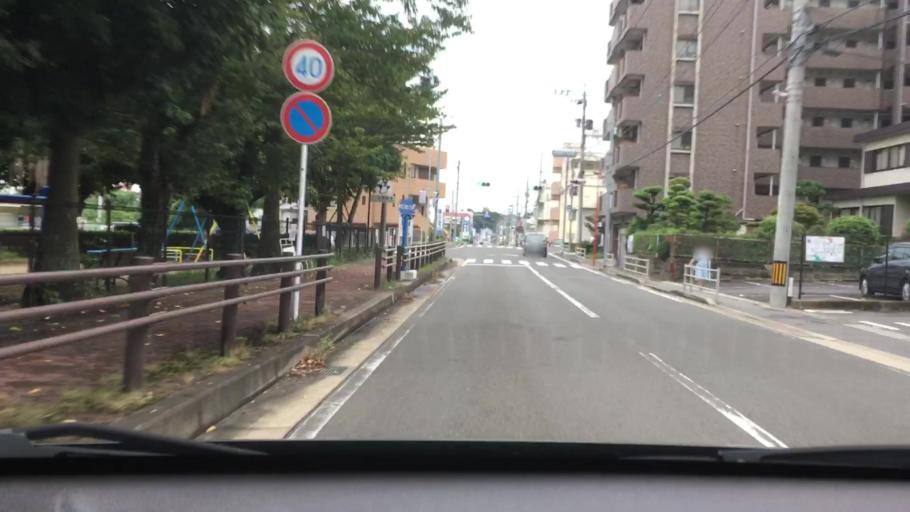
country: JP
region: Nagasaki
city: Nagasaki-shi
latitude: 32.7589
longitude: 129.9422
